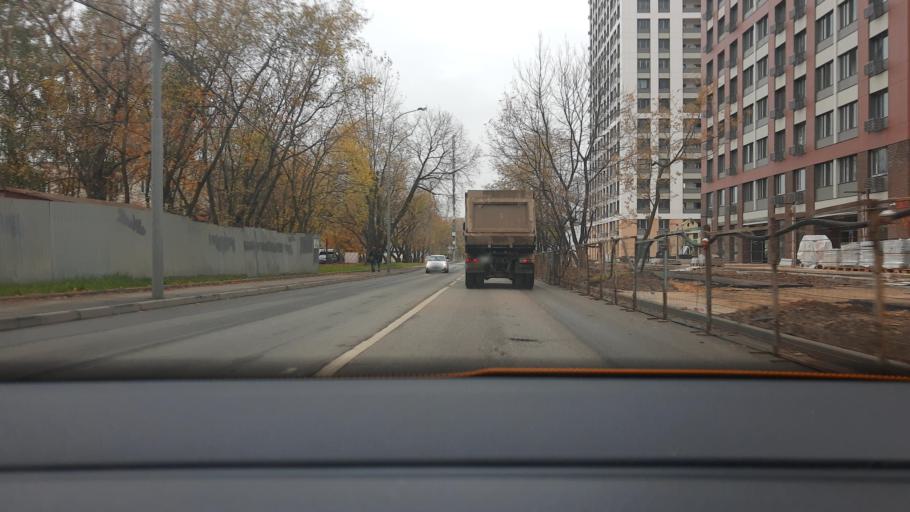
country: RU
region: Moscow
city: Metrogorodok
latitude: 55.8188
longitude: 37.7526
